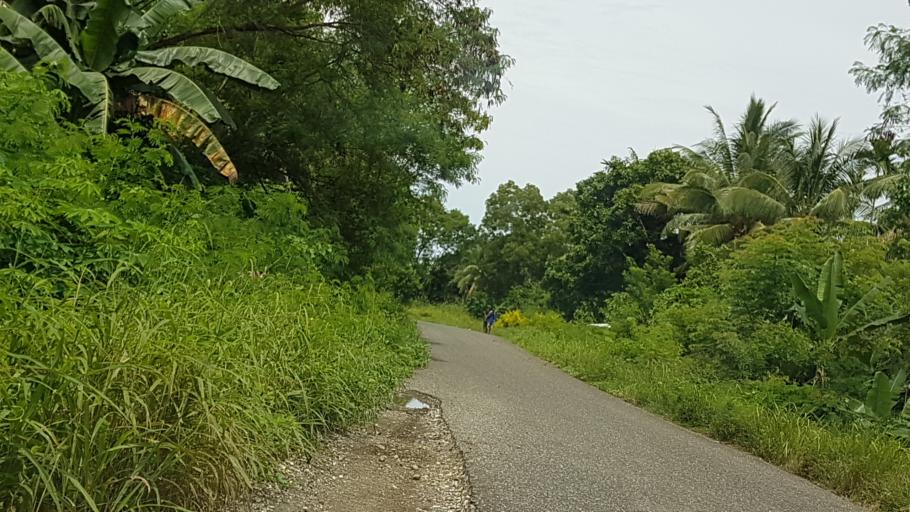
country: PG
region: Madang
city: Madang
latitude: -4.5917
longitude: 145.5403
